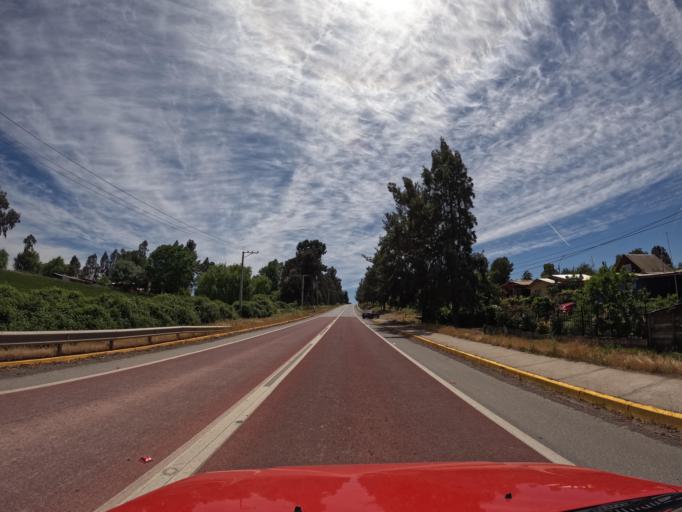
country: CL
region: Maule
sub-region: Provincia de Talca
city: Talca
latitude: -35.3012
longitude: -71.5237
